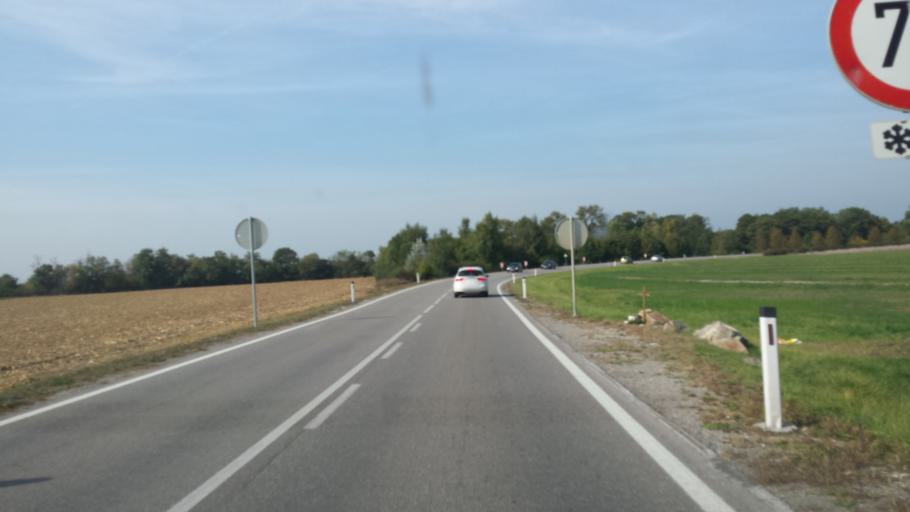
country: AT
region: Lower Austria
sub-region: Politischer Bezirk Tulln
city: Langenrohr
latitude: 48.3163
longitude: 16.0336
